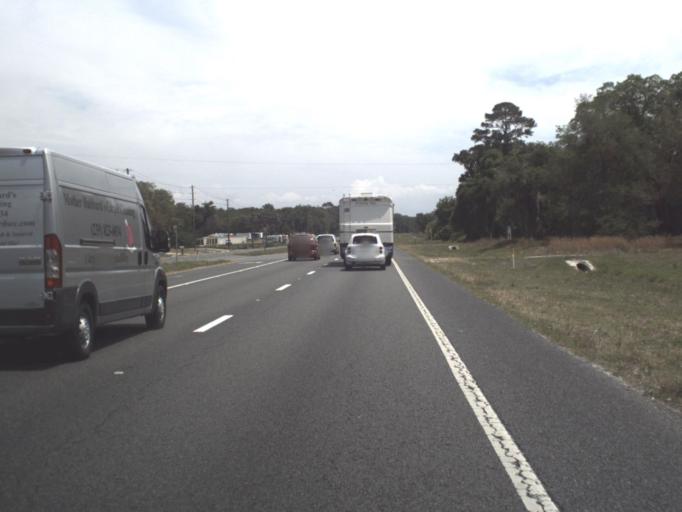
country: US
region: Florida
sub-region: Sumter County
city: Wildwood
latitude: 28.8376
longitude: -82.0118
